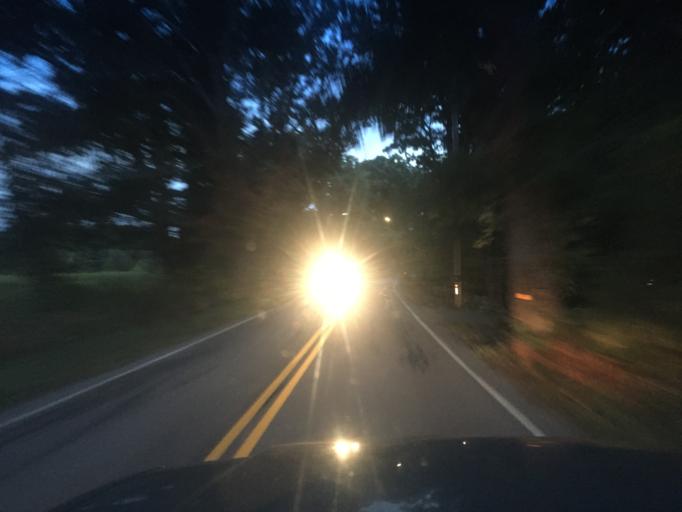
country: US
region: Massachusetts
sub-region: Norfolk County
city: Millis
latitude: 42.1821
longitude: -71.3708
